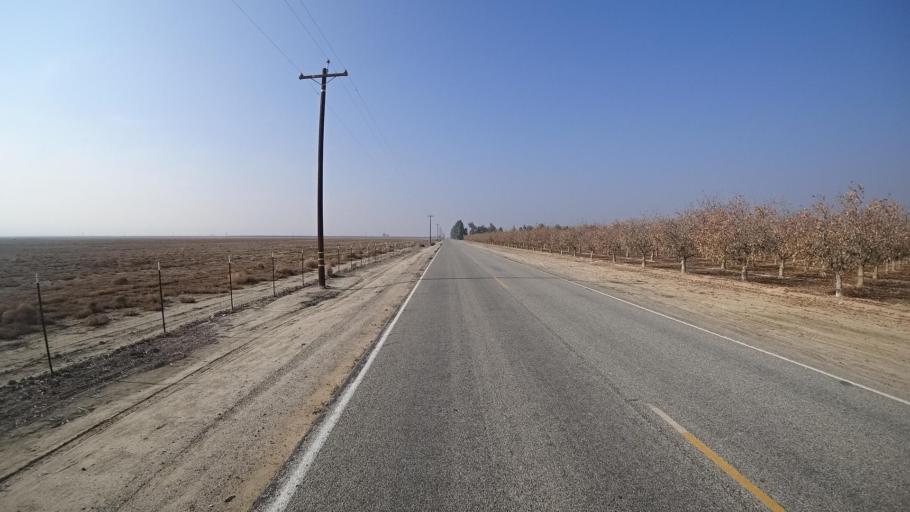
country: US
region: California
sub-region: Kern County
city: Buttonwillow
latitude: 35.3548
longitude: -119.3617
